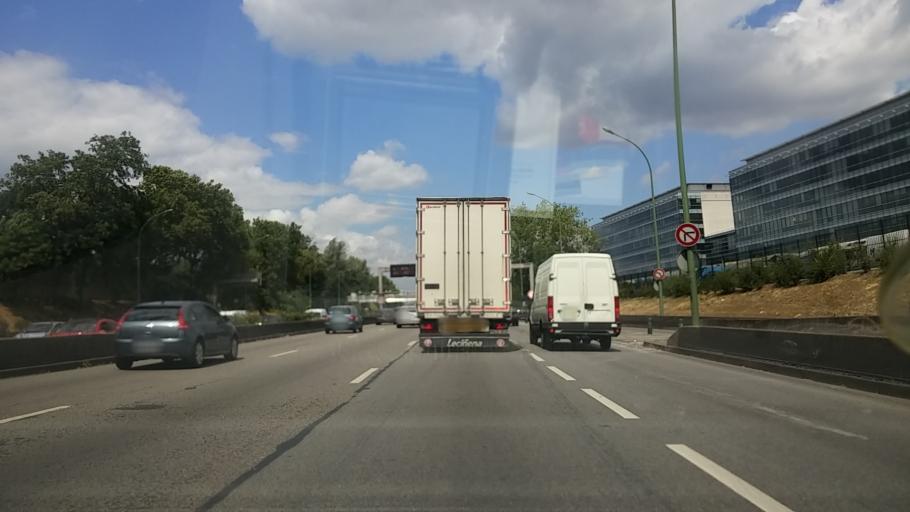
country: FR
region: Ile-de-France
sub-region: Departement de Seine-Saint-Denis
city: Bagnolet
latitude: 48.8557
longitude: 2.4142
